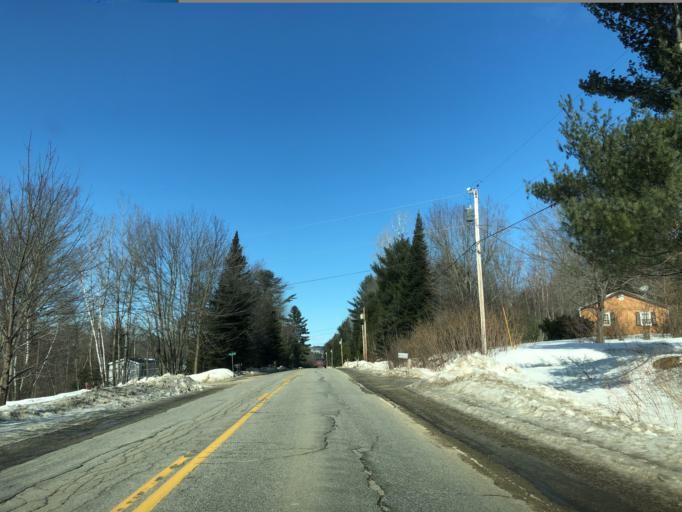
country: US
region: Maine
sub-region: Oxford County
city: Buckfield
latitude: 44.2501
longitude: -70.3373
